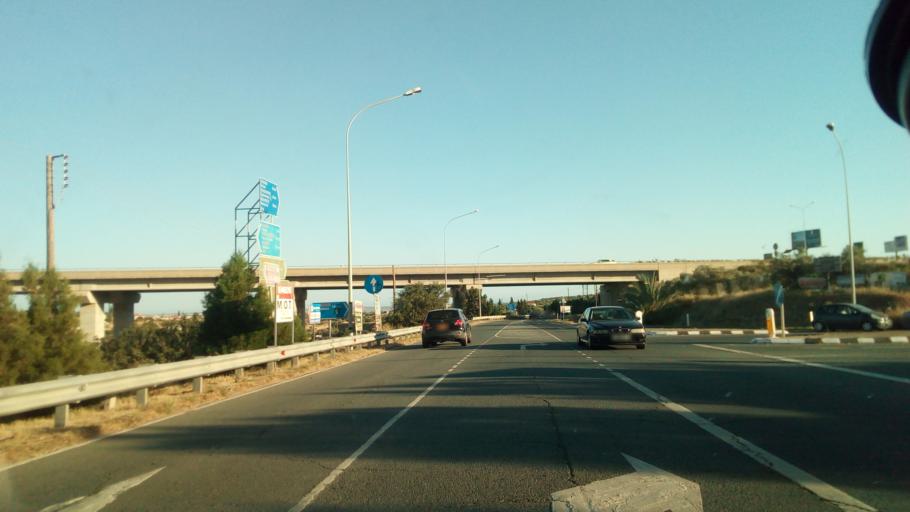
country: CY
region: Limassol
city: Erimi
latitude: 34.6863
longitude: 32.9095
